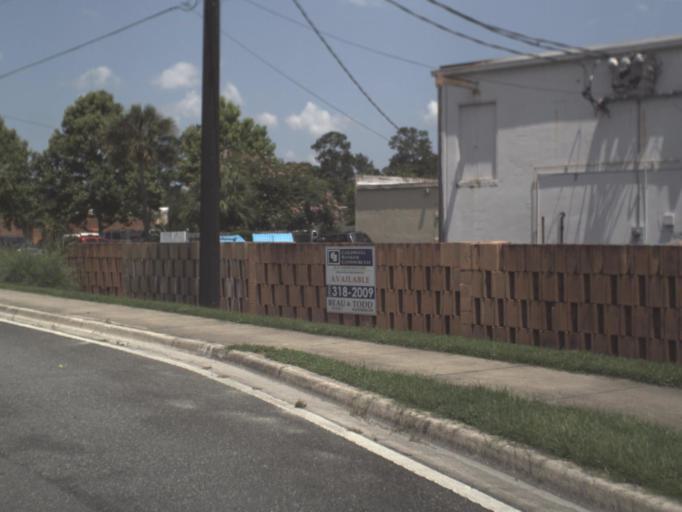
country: US
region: Florida
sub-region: Alachua County
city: Gainesville
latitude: 29.6506
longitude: -82.3742
